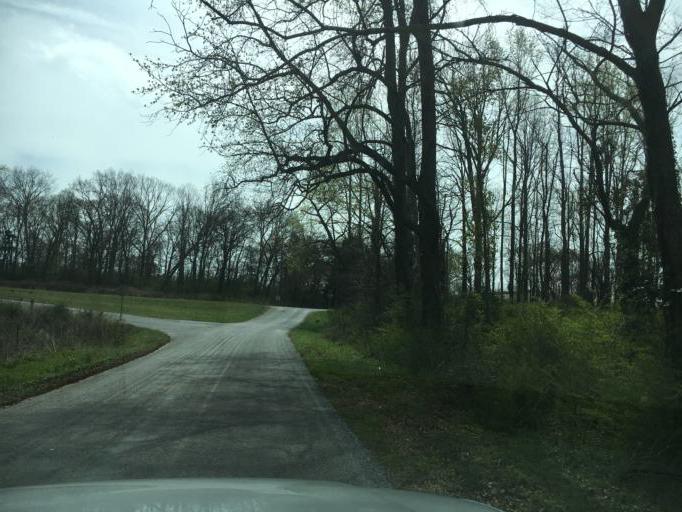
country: US
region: Georgia
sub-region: Hart County
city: Royston
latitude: 34.3582
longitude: -83.0465
